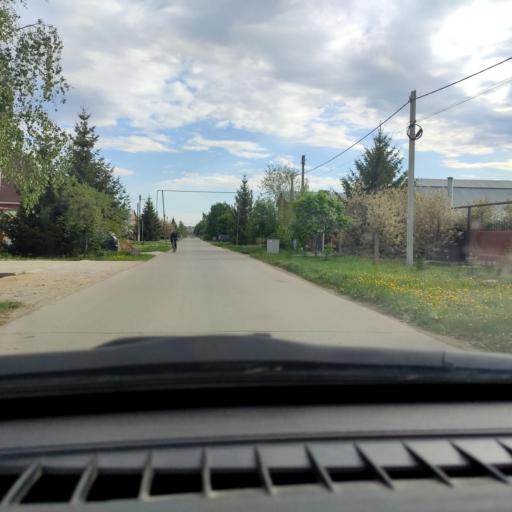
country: RU
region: Samara
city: Tol'yatti
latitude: 53.5620
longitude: 49.4027
